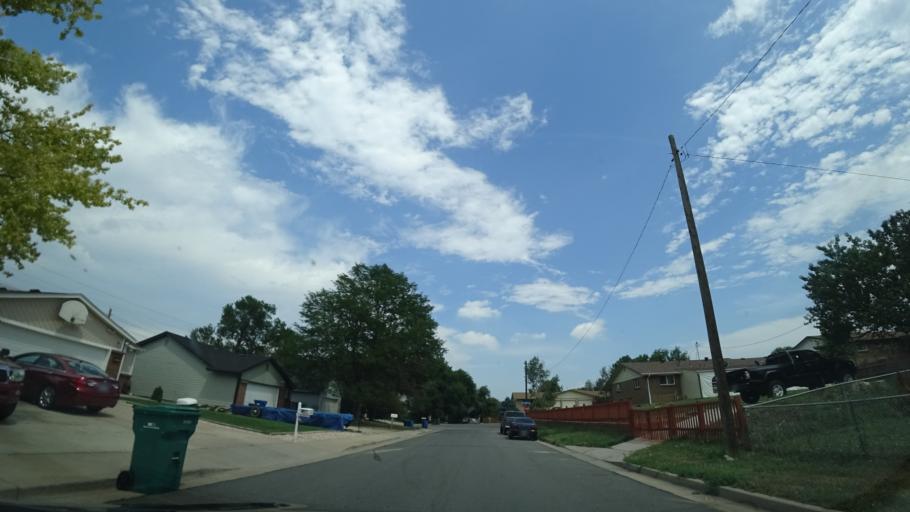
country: US
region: Colorado
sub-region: Jefferson County
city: Lakewood
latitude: 39.6999
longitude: -105.0758
